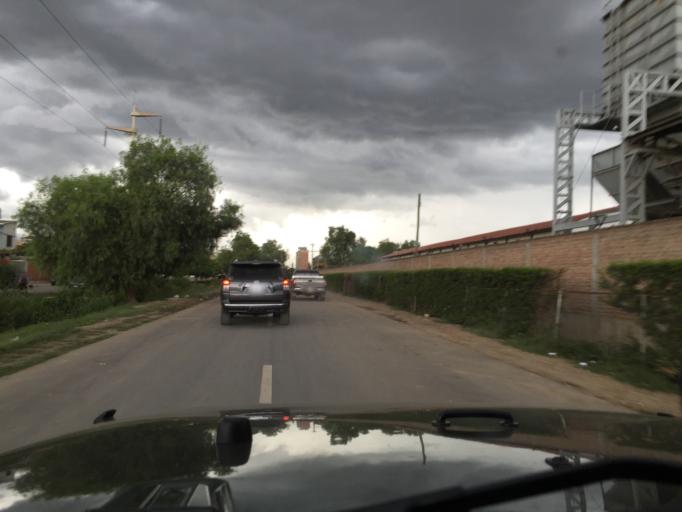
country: BO
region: Cochabamba
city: Cochabamba
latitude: -17.4001
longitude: -66.1967
